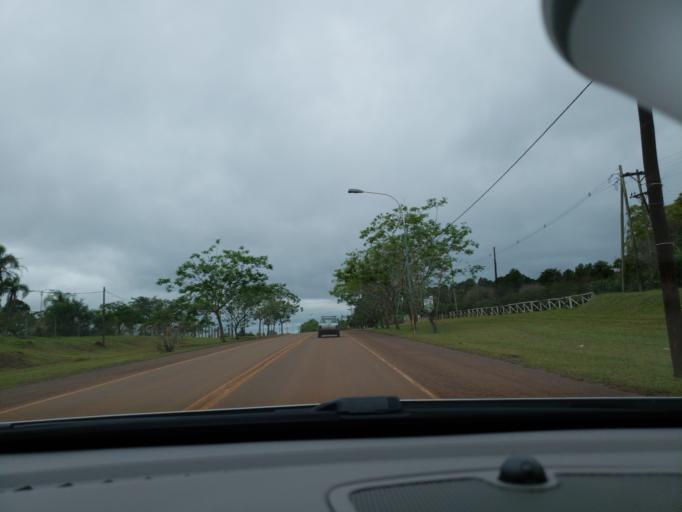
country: AR
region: Misiones
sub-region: Departamento de Apostoles
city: Apostoles
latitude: -27.8960
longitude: -55.7605
